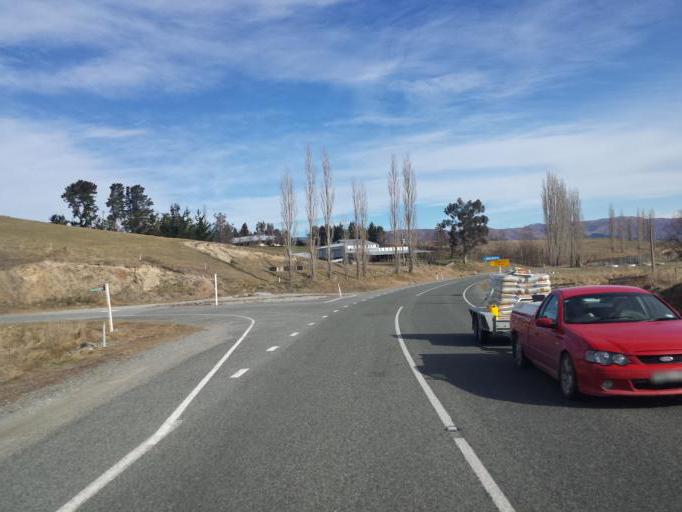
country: NZ
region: Canterbury
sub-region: Timaru District
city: Pleasant Point
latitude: -44.0657
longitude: 170.8831
